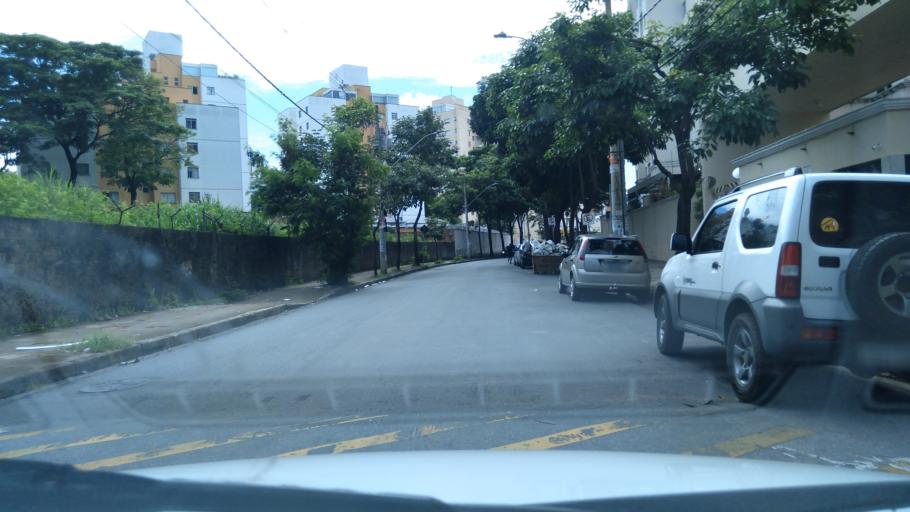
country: BR
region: Minas Gerais
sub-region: Belo Horizonte
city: Belo Horizonte
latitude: -19.8725
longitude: -43.9231
